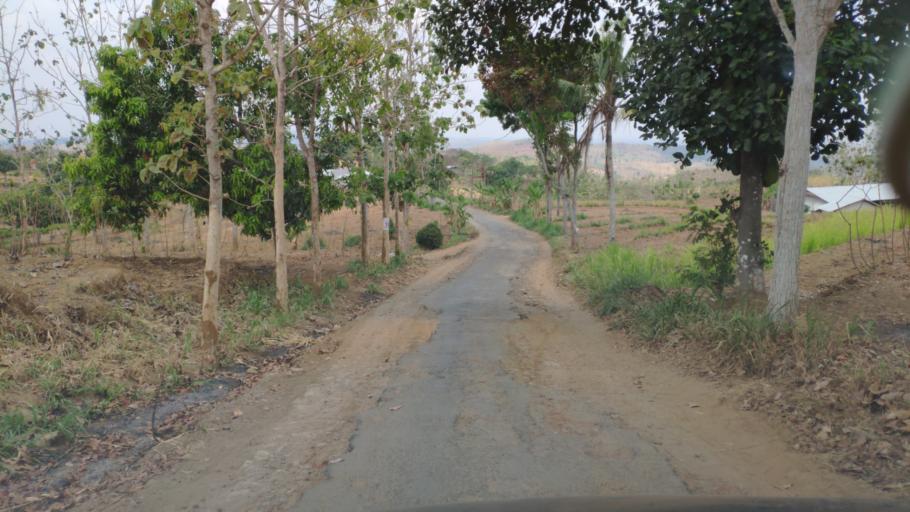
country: ID
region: Central Java
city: Koro
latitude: -6.9023
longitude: 111.2185
